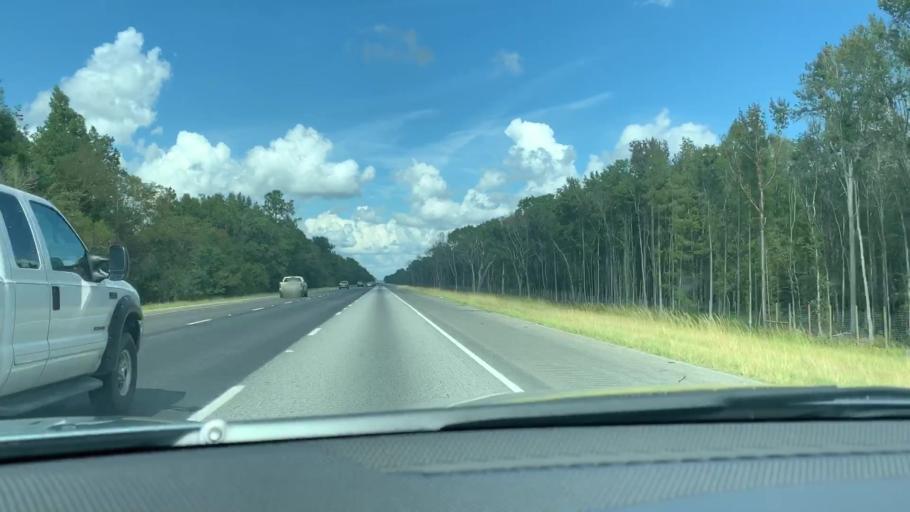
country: US
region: Georgia
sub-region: Camden County
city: Woodbine
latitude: 30.8871
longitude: -81.6857
